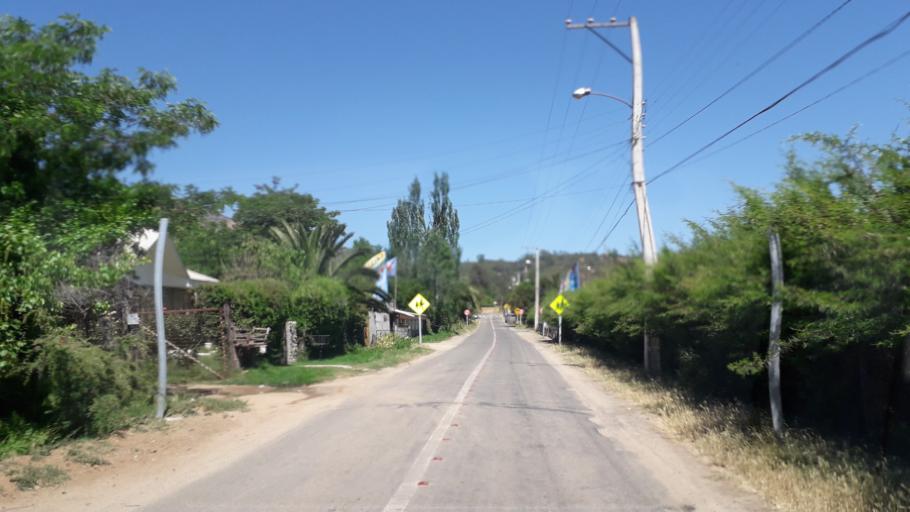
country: CL
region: Valparaiso
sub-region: Provincia de Marga Marga
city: Limache
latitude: -33.0632
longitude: -71.2219
